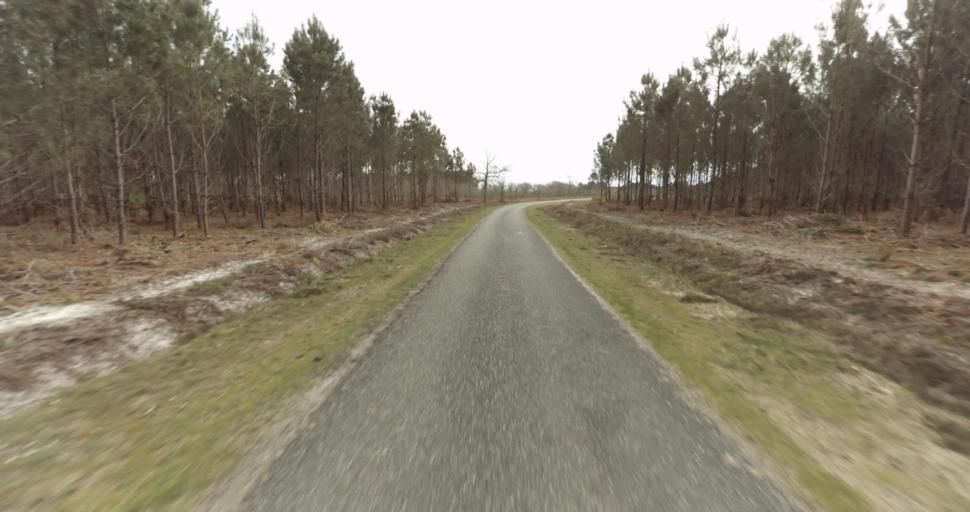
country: FR
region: Aquitaine
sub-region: Departement des Landes
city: Sarbazan
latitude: 44.0162
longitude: -0.3004
